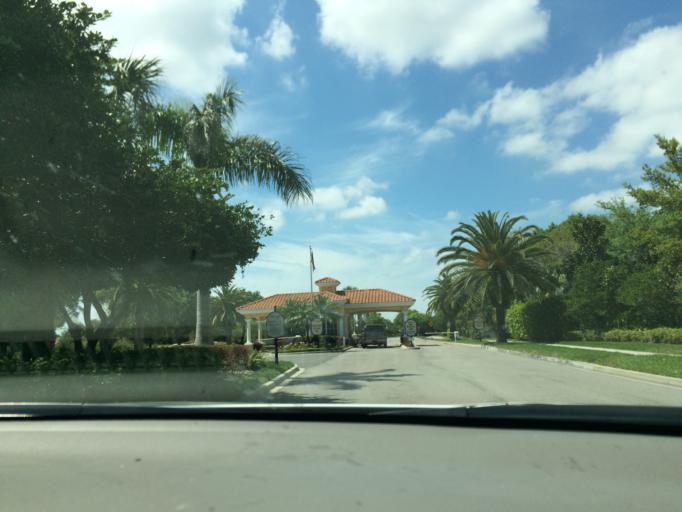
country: US
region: Florida
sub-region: Manatee County
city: Ellenton
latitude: 27.5085
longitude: -82.4351
